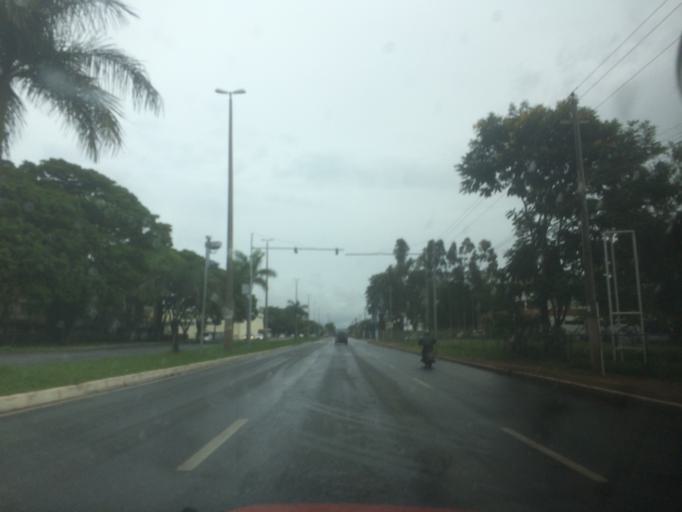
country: BR
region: Federal District
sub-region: Brasilia
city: Brasilia
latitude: -15.7613
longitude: -47.8774
